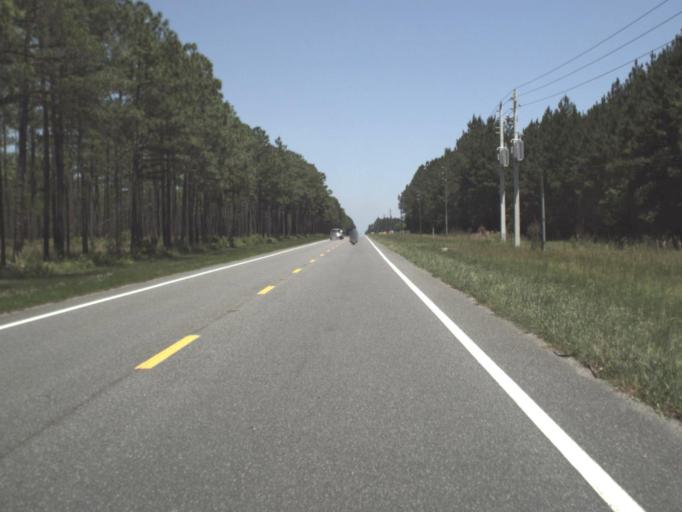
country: US
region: Florida
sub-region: Columbia County
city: Watertown
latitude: 30.1929
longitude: -82.5150
